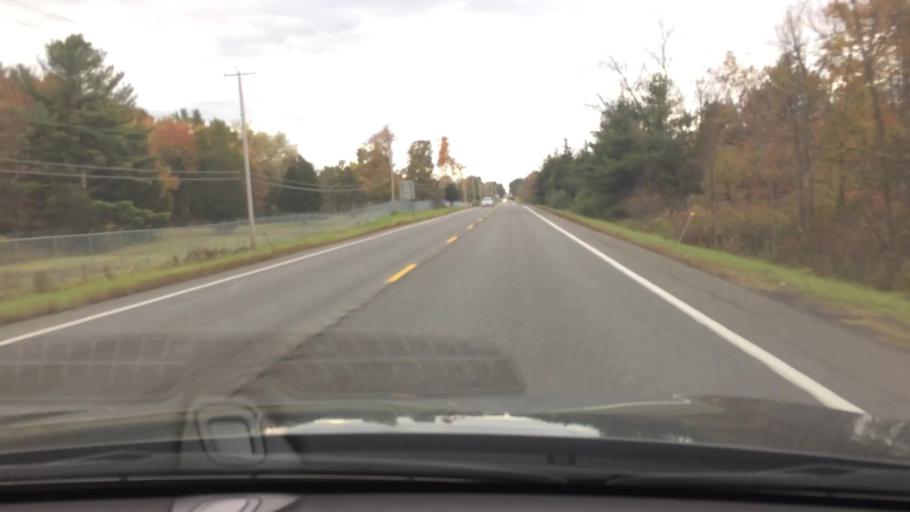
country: US
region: New York
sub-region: Columbia County
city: Stottville
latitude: 42.2933
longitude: -73.7145
